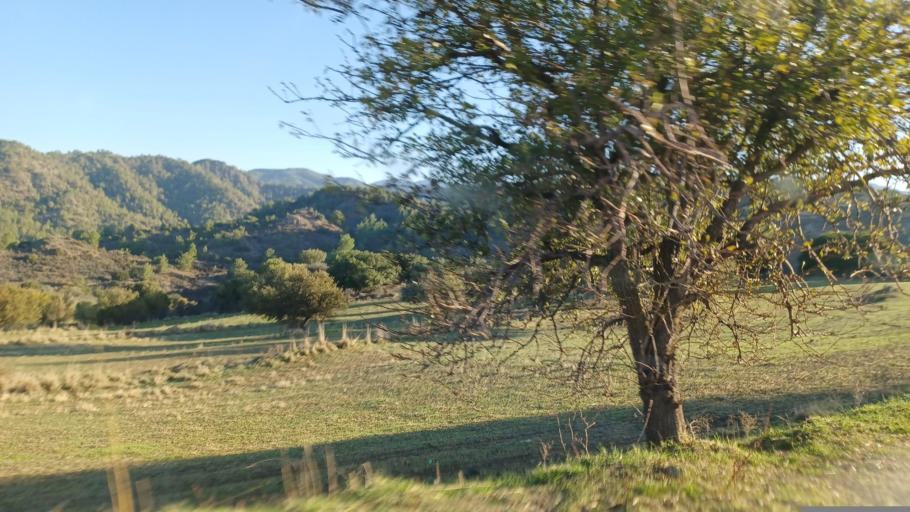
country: CY
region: Pafos
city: Polis
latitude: 34.9484
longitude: 32.5572
